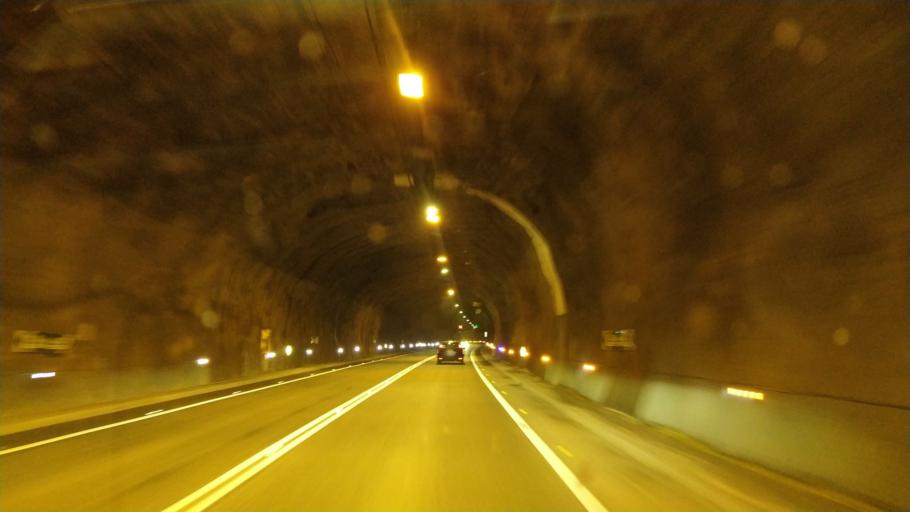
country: ES
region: Catalonia
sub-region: Provincia de Lleida
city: Coll de Nargo
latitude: 42.2525
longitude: 1.3489
